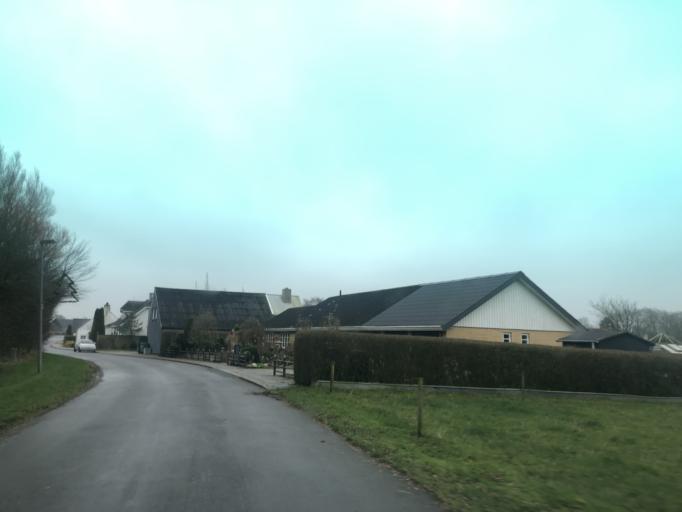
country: DK
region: Central Jutland
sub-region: Struer Kommune
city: Struer
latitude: 56.4366
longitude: 8.5835
